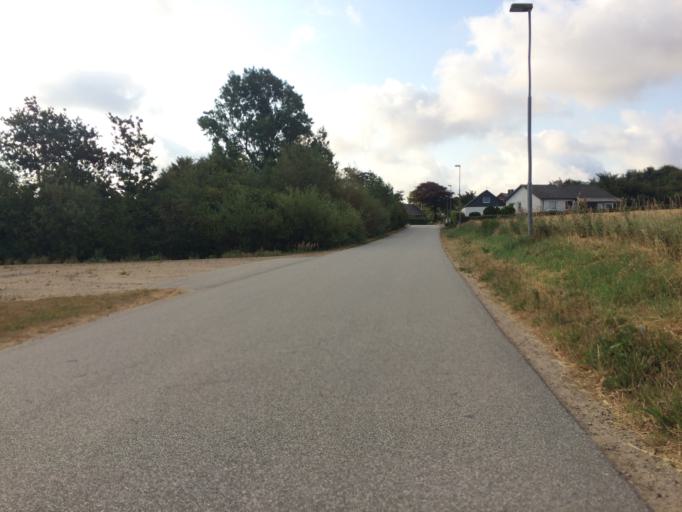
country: DK
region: Central Jutland
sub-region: Holstebro Kommune
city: Vinderup
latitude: 56.6062
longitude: 8.8077
